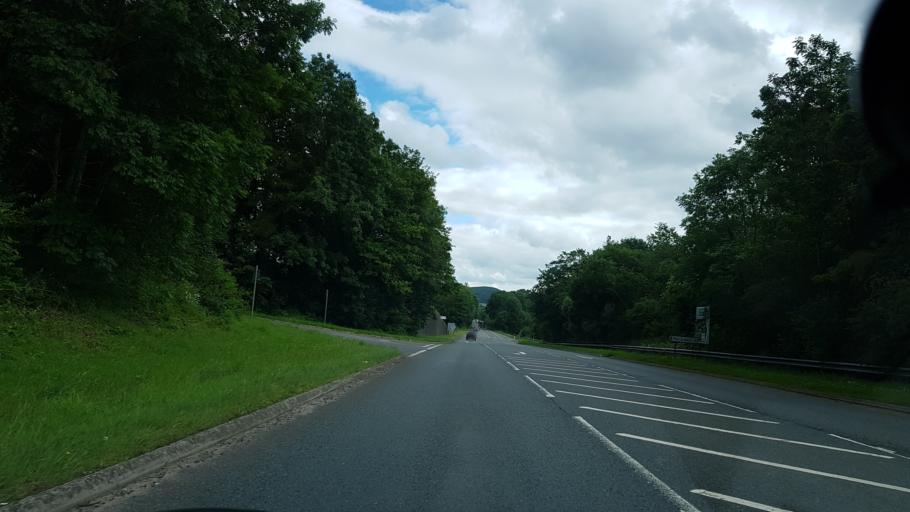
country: GB
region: Wales
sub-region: Monmouthshire
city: Abergavenny
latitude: 51.8518
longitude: -3.0019
